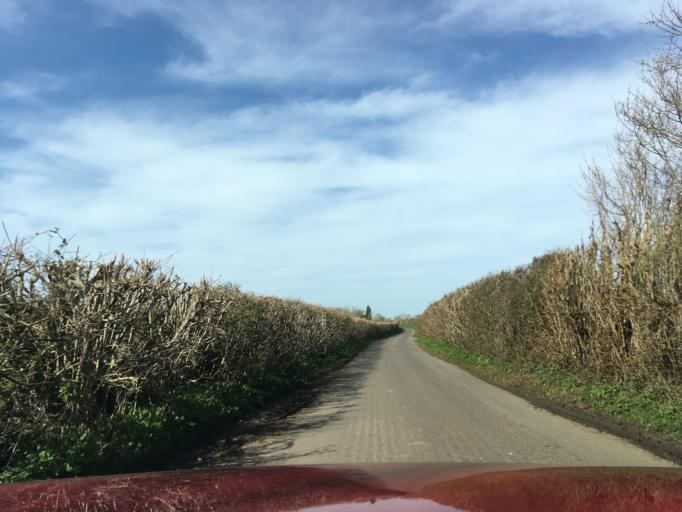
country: GB
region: England
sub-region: Wiltshire
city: Chippenham
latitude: 51.4838
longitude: -2.1600
